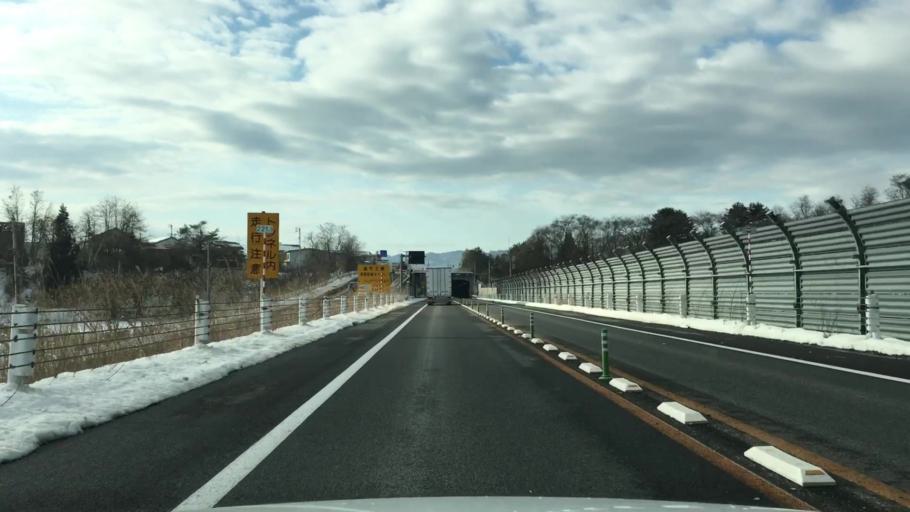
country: JP
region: Akita
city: Odate
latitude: 40.2784
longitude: 140.5368
